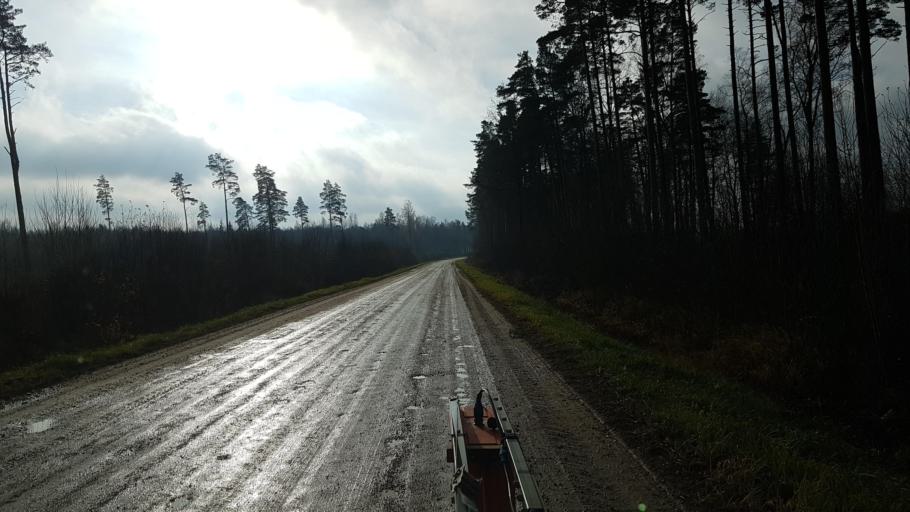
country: EE
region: Raplamaa
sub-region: Maerjamaa vald
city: Marjamaa
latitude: 58.8679
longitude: 24.2299
